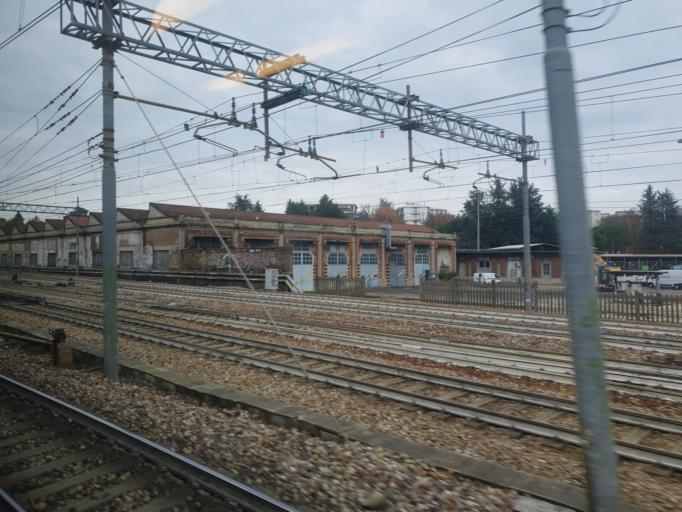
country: IT
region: Lombardy
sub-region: Provincia di Varese
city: Saronno
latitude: 45.6271
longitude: 9.0276
